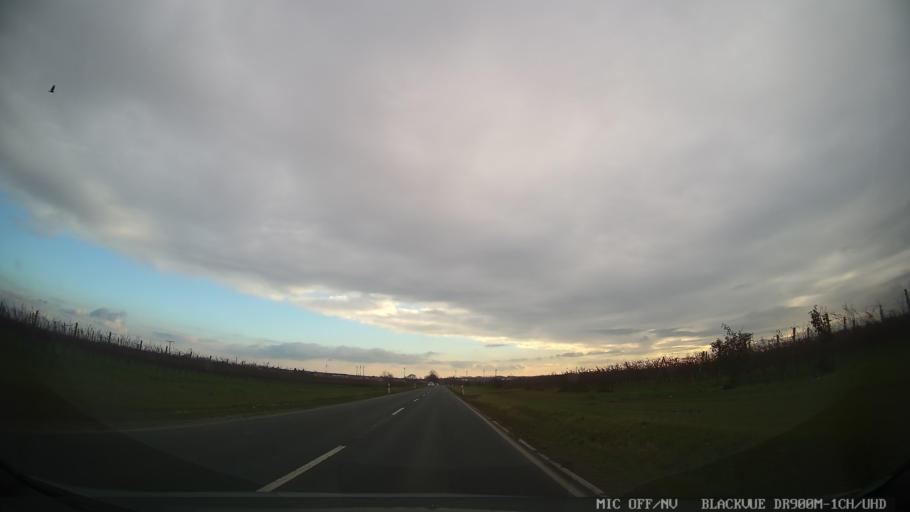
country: DE
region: Rheinland-Pfalz
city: Weinolsheim
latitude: 49.8235
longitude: 8.2663
